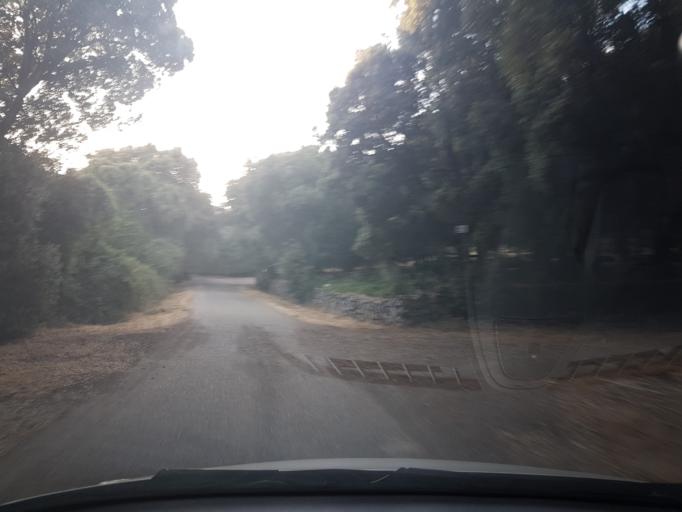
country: IT
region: Sardinia
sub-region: Provincia di Oristano
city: Seneghe
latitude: 40.1125
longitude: 8.5841
